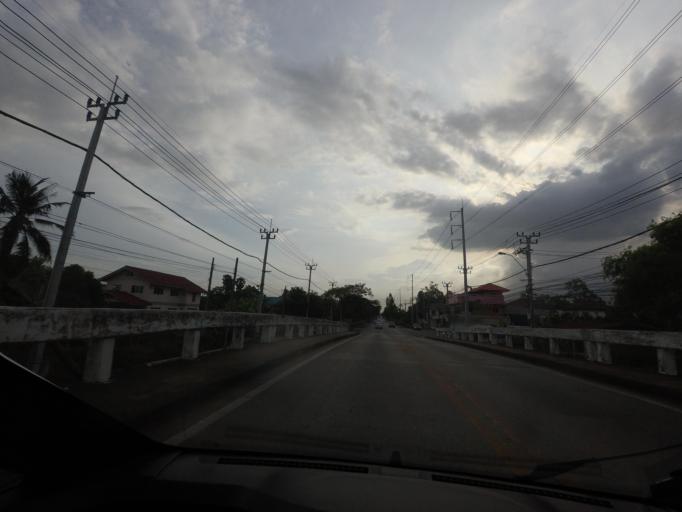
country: TH
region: Bangkok
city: Nong Chok
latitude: 13.8584
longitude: 100.8427
